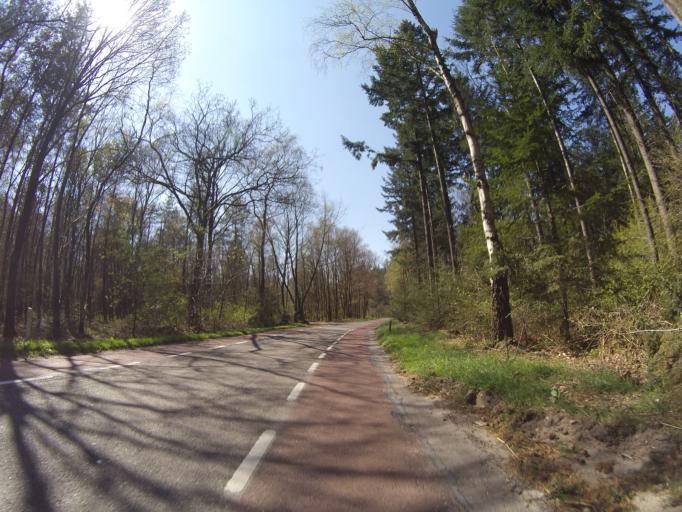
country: NL
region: Utrecht
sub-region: Gemeente Utrechtse Heuvelrug
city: Overberg
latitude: 52.0303
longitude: 5.4875
